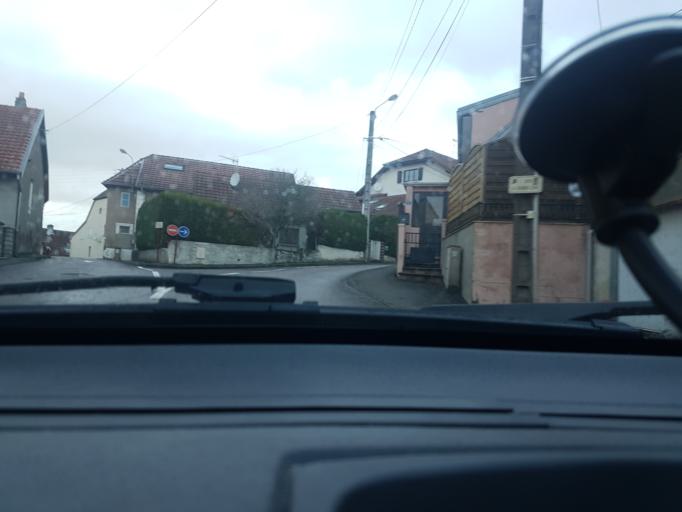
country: FR
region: Franche-Comte
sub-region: Territoire de Belfort
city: Bavilliers
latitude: 47.6221
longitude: 6.8331
